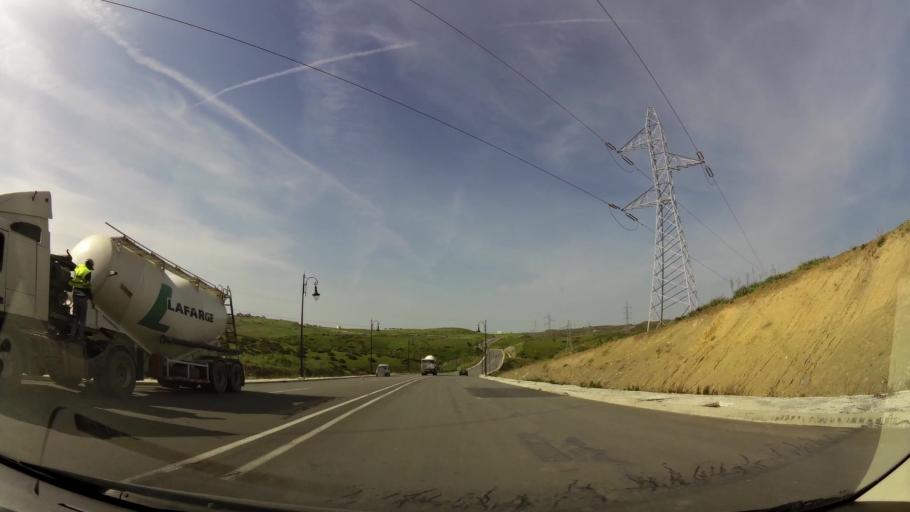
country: MA
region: Tanger-Tetouan
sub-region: Tanger-Assilah
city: Tangier
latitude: 35.7155
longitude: -5.7740
